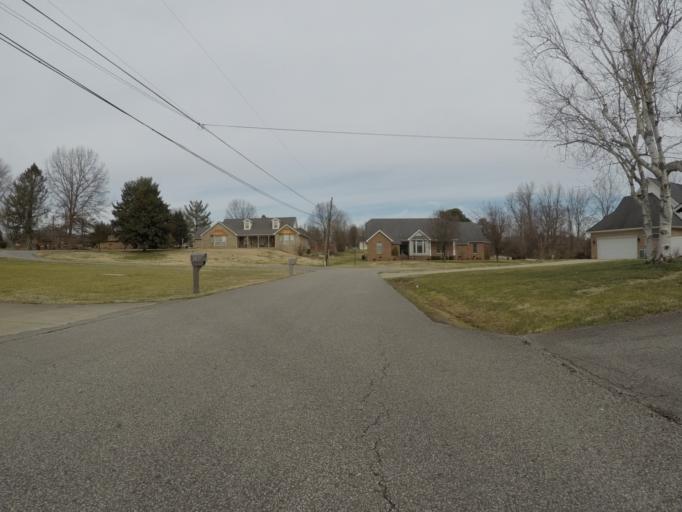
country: US
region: West Virginia
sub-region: Cabell County
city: Pea Ridge
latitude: 38.4454
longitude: -82.3512
